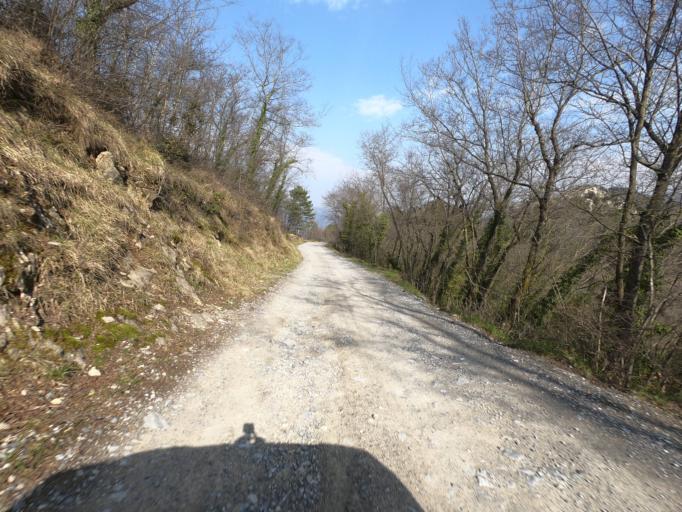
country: IT
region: Liguria
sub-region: Provincia di Savona
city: Balestrino
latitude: 44.1151
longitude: 8.1454
